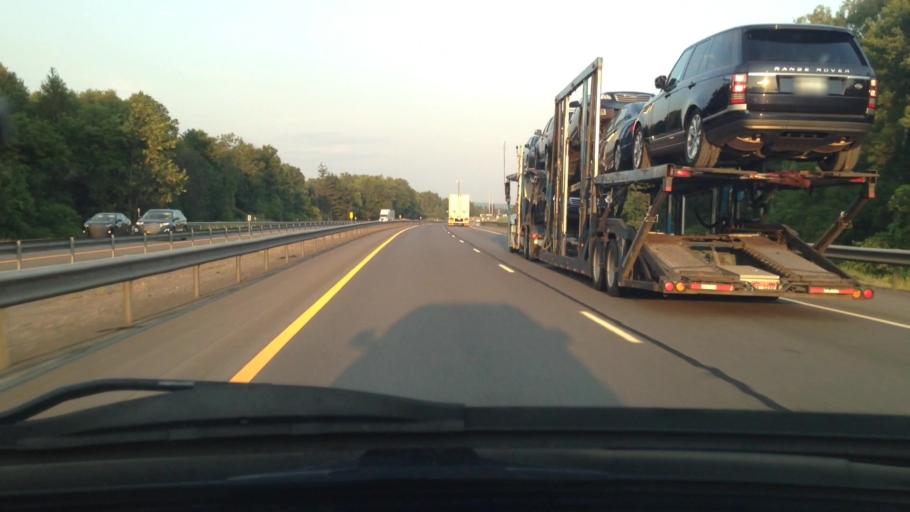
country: US
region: New York
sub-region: Oneida County
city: Utica
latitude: 43.1082
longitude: -75.1789
